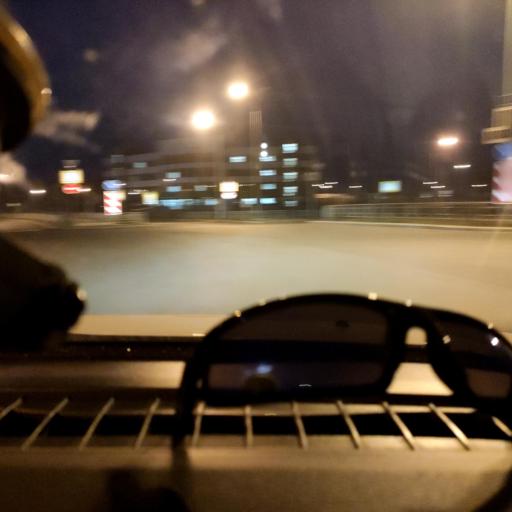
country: RU
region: Samara
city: Samara
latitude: 53.0959
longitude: 50.1723
